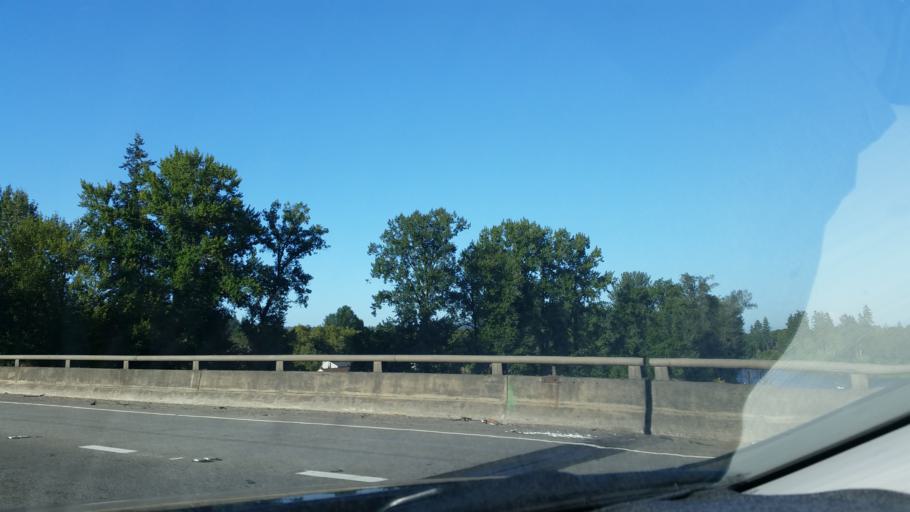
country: US
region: Oregon
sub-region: Clackamas County
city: Wilsonville
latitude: 45.2919
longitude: -122.7693
